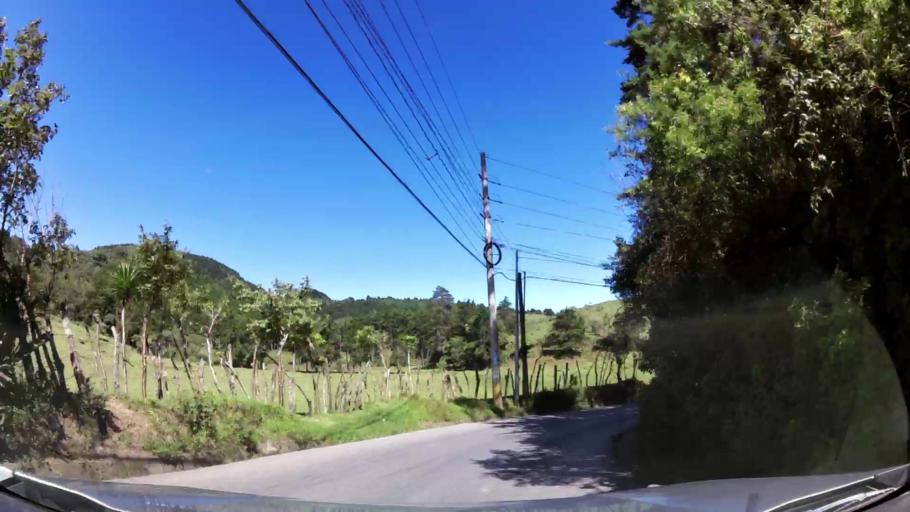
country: GT
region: Guatemala
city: San Jose Pinula
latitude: 14.5222
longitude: -90.4216
